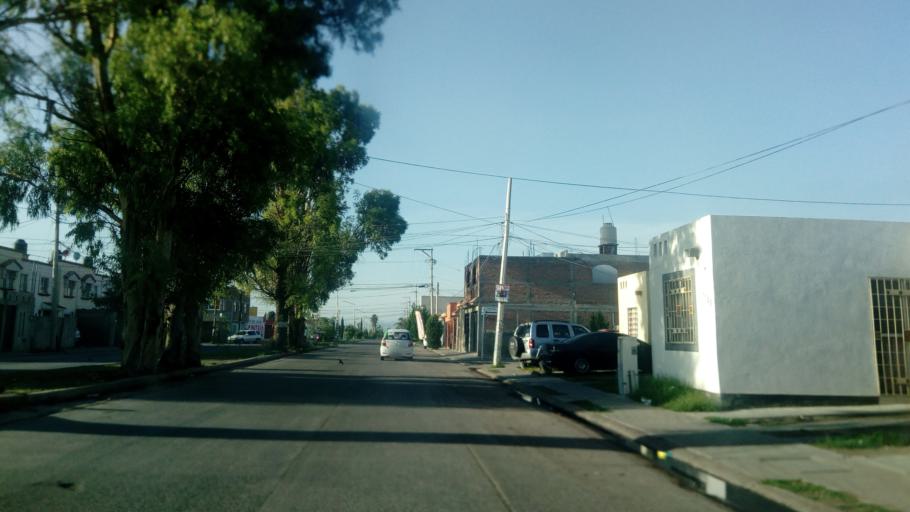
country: MX
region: Durango
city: Victoria de Durango
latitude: 24.0740
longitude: -104.5877
